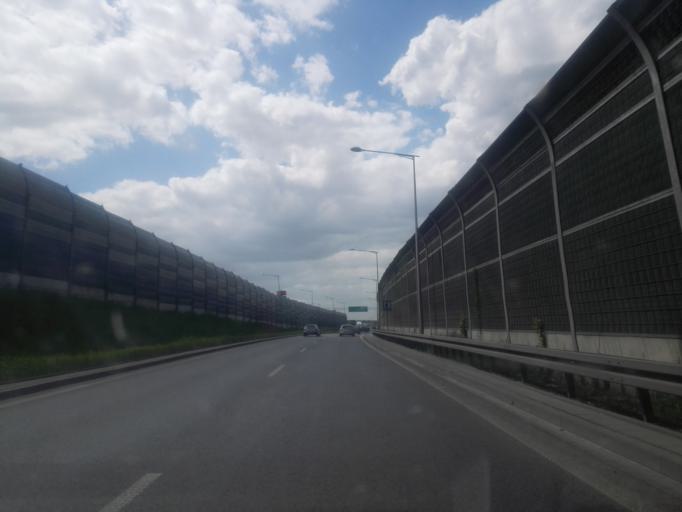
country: PL
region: Masovian Voivodeship
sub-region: Powiat wolominski
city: Marki
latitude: 52.3076
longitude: 21.0894
